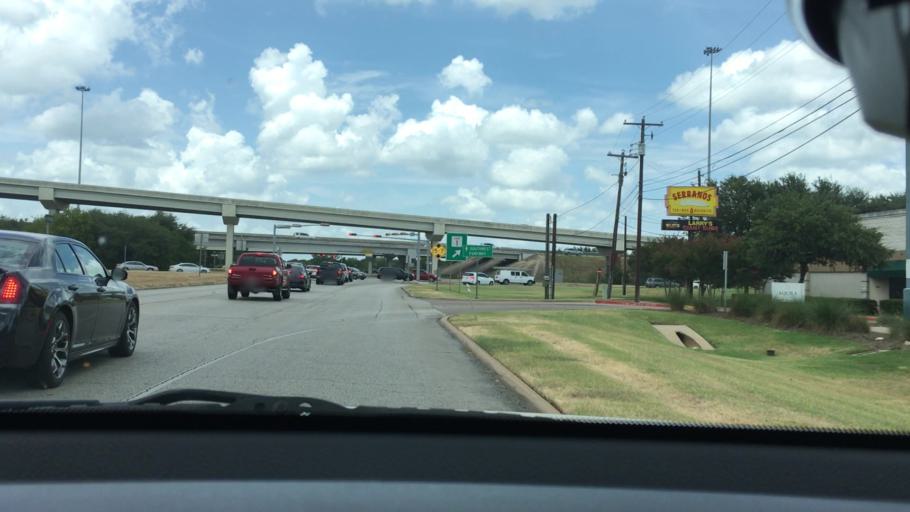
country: US
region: Texas
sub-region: Travis County
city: Rollingwood
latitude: 30.2355
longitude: -97.8220
